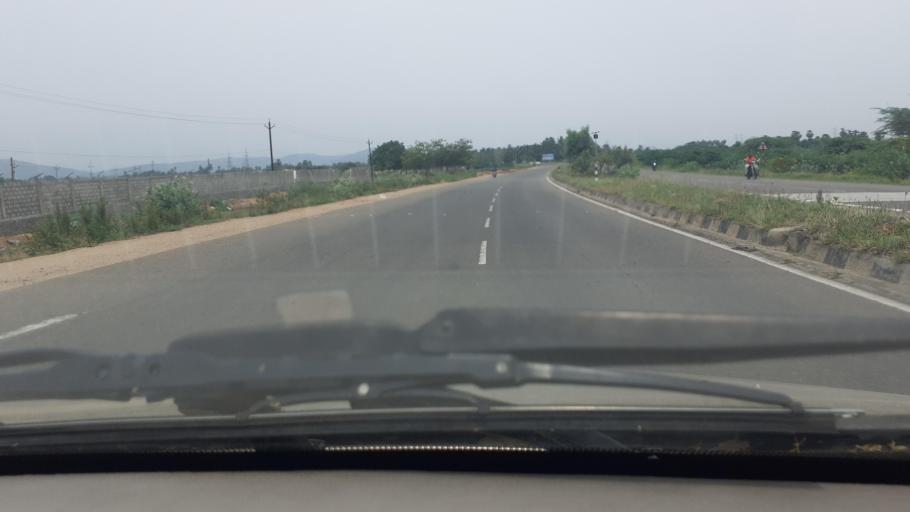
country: IN
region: Tamil Nadu
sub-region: Tirunelveli Kattabo
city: Tirunelveli
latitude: 8.7102
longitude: 77.8083
